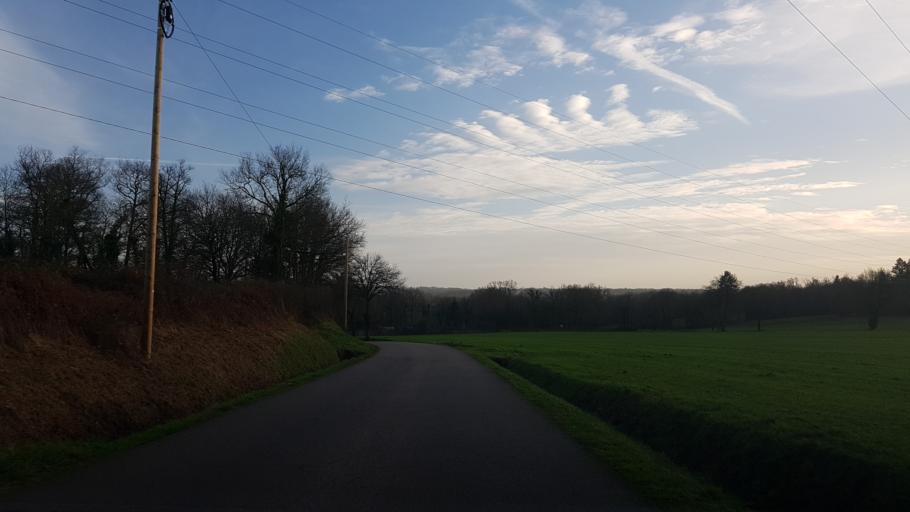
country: FR
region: Limousin
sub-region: Departement de la Haute-Vienne
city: Saint-Junien
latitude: 45.9023
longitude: 0.8558
